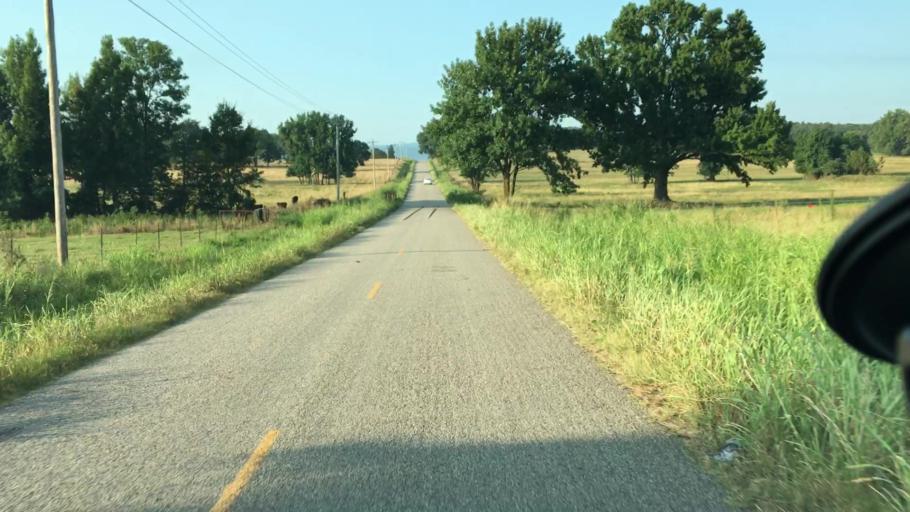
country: US
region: Arkansas
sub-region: Johnson County
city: Coal Hill
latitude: 35.3557
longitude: -93.6132
